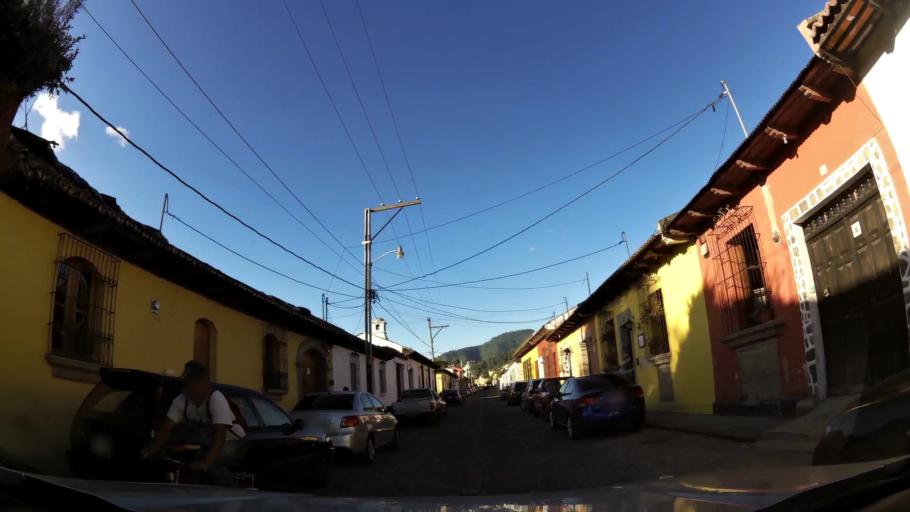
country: GT
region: Sacatepequez
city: Antigua Guatemala
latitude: 14.5538
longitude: -90.7343
